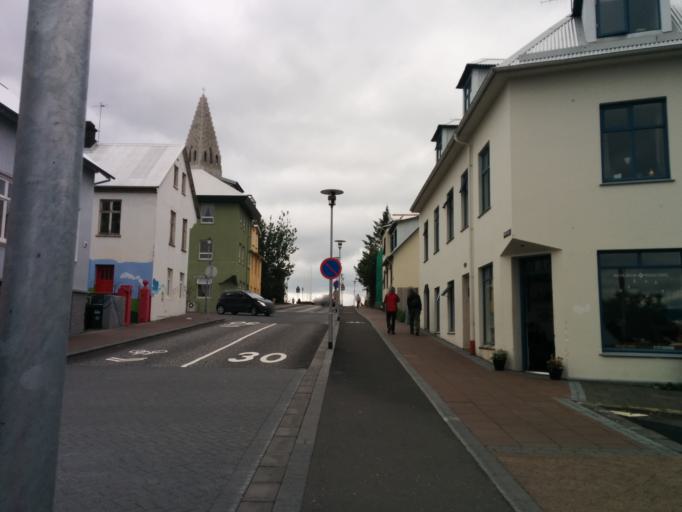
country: IS
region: Capital Region
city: Reykjavik
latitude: 64.1436
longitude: -21.9264
